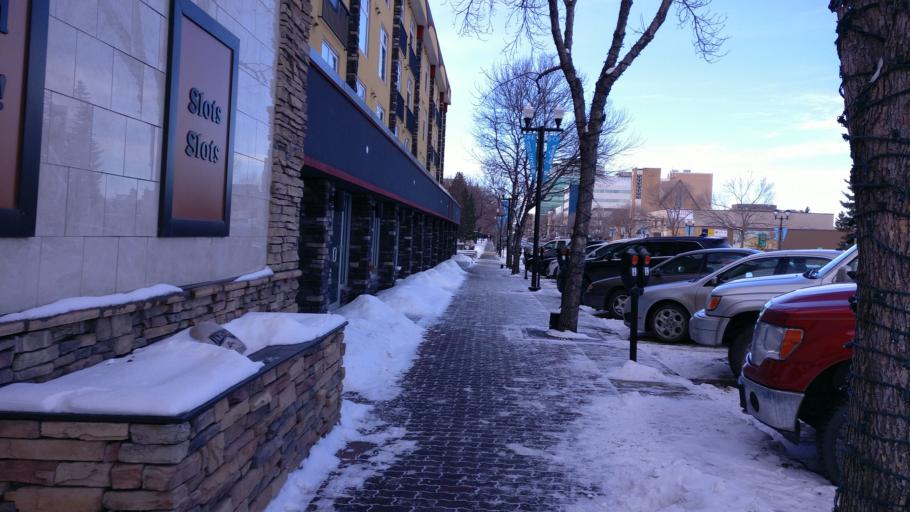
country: CA
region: Alberta
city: Red Deer
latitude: 52.2688
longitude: -113.8055
